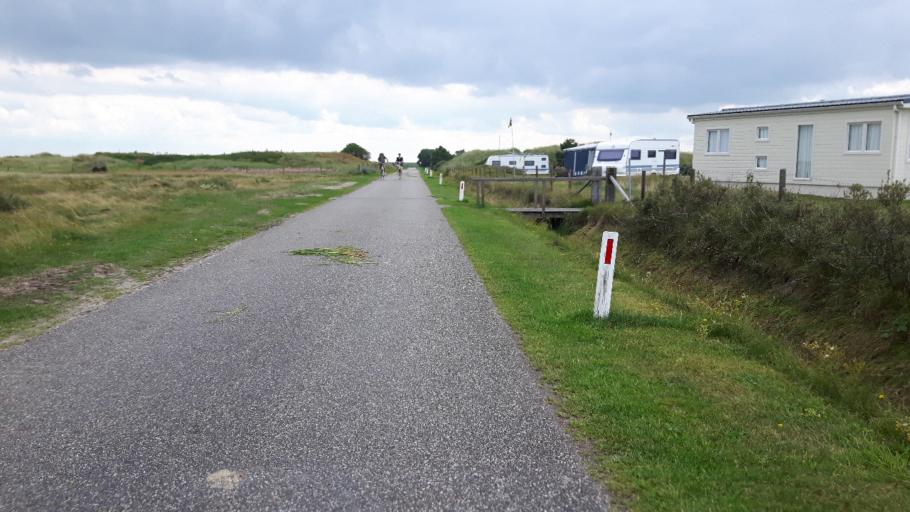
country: NL
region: Friesland
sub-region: Gemeente Ameland
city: Nes
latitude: 53.4526
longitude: 5.8172
